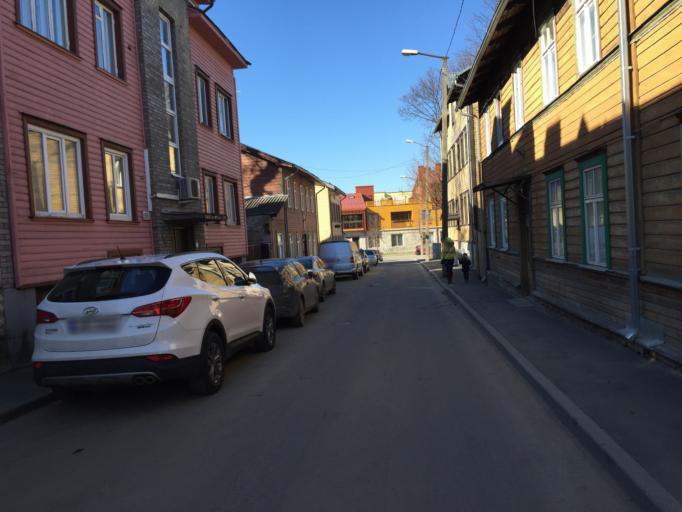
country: EE
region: Harju
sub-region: Tallinna linn
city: Tallinn
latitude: 59.4484
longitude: 24.7378
